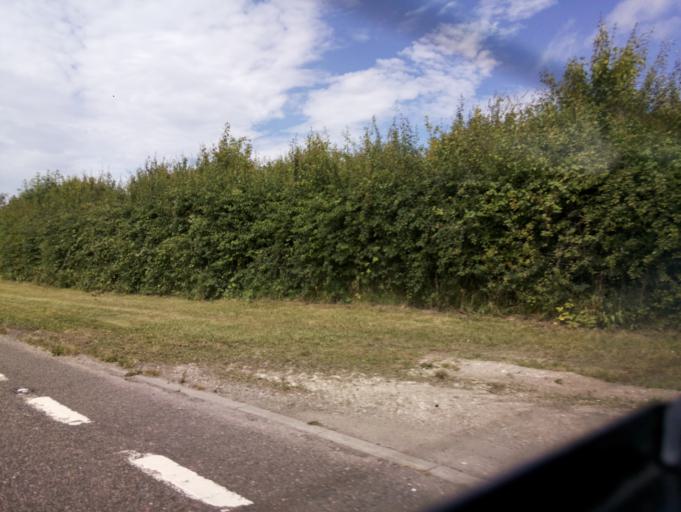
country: GB
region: England
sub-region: Dorset
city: Sherborne
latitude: 50.8203
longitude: -2.5573
